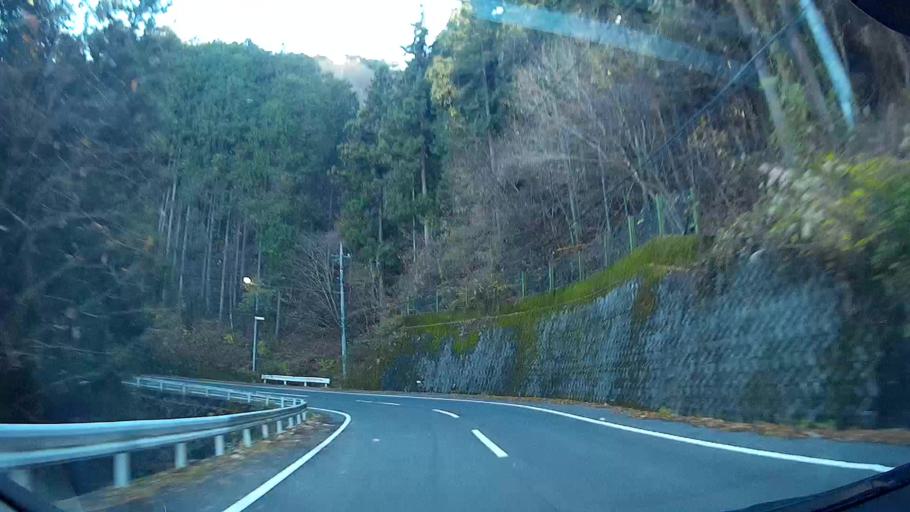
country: JP
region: Yamanashi
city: Otsuki
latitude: 35.7480
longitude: 138.9559
